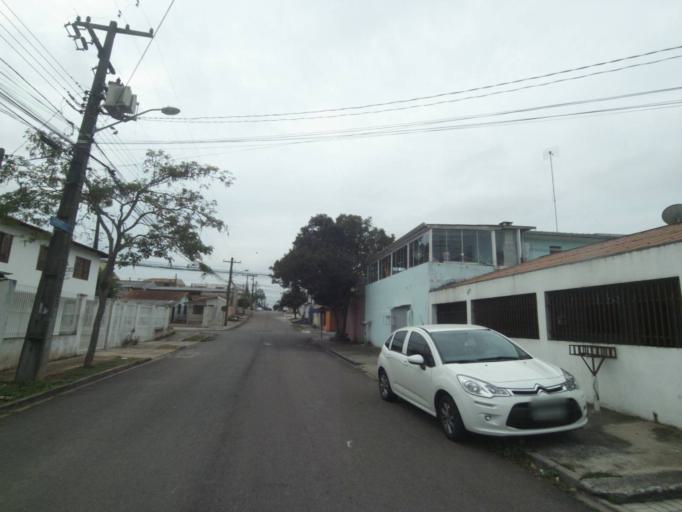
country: BR
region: Parana
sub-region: Sao Jose Dos Pinhais
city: Sao Jose dos Pinhais
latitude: -25.5509
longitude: -49.2619
